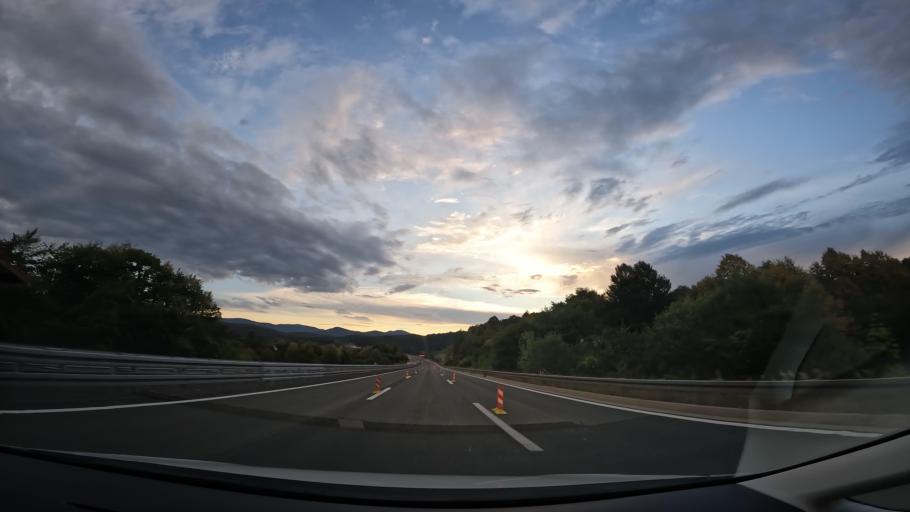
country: HR
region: Primorsko-Goranska
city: Vrbovsko
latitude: 45.3778
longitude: 15.1437
